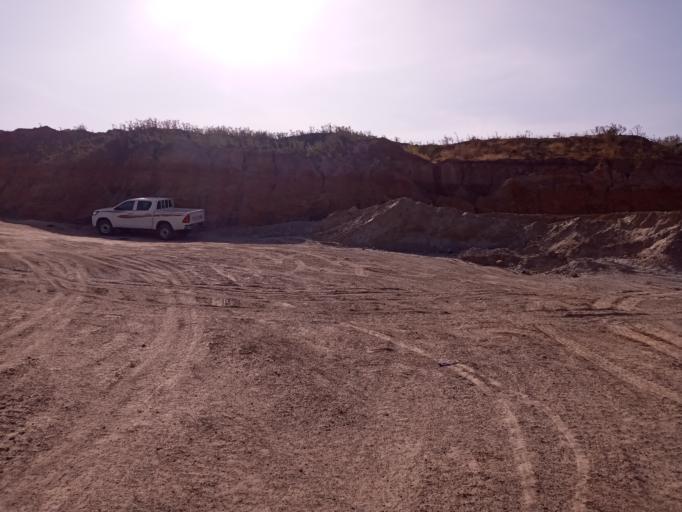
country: ET
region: Oromiya
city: Shashemene
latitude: 7.3160
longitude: 38.6258
